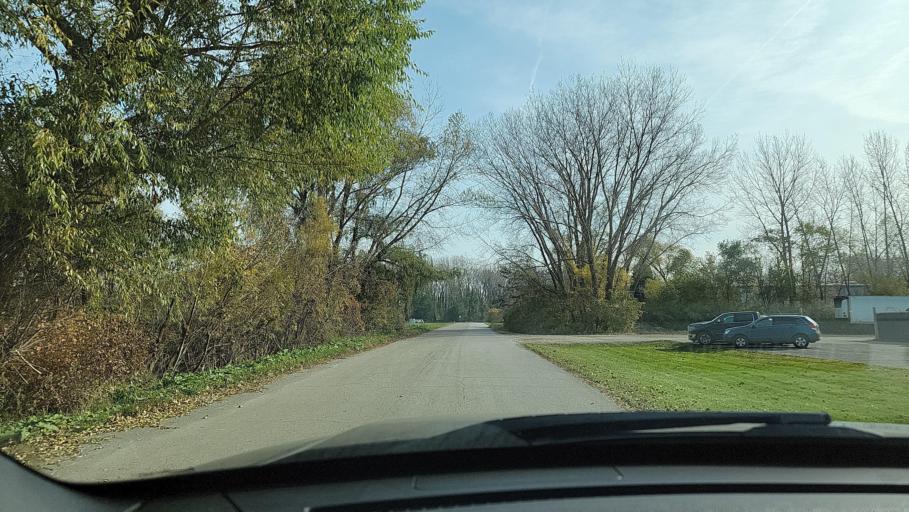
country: US
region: Indiana
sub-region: Porter County
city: Ogden Dunes
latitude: 41.6145
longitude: -87.1632
